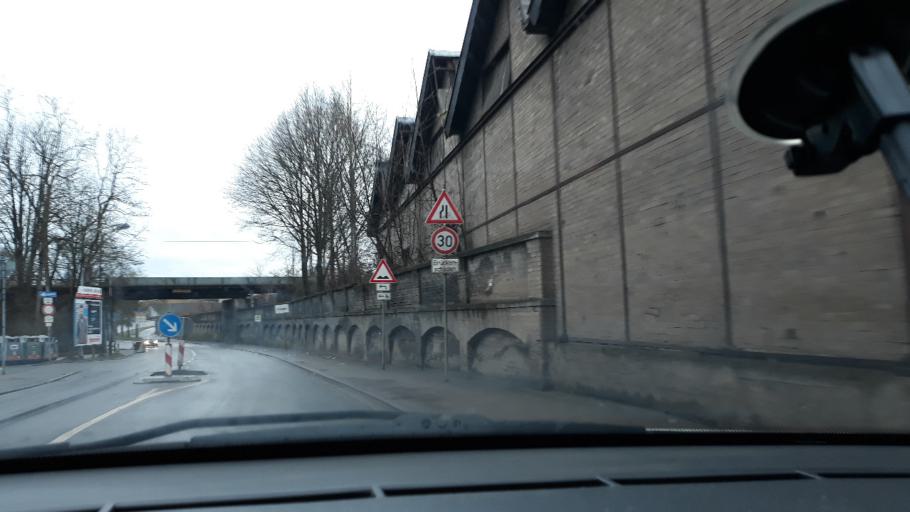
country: FR
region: Lorraine
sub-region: Departement de la Moselle
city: Alsting
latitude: 49.2116
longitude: 7.0321
